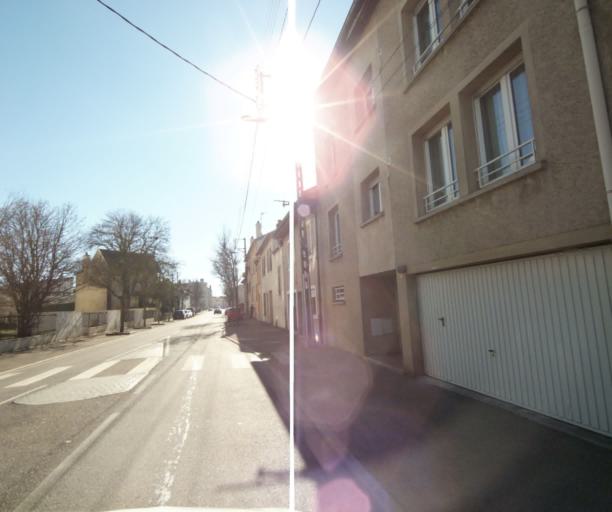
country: FR
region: Lorraine
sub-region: Departement de Meurthe-et-Moselle
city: Tomblaine
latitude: 48.6900
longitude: 6.2104
